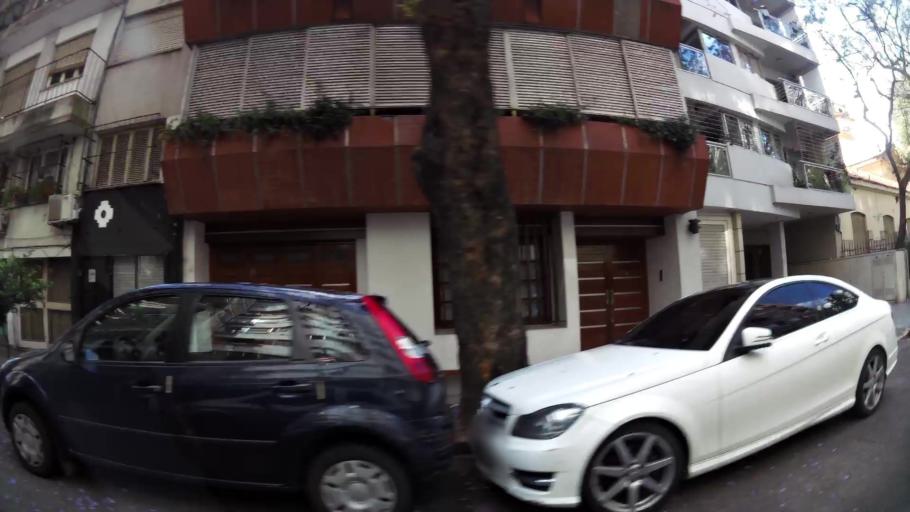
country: AR
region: Santa Fe
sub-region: Departamento de Rosario
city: Rosario
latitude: -32.9554
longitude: -60.6258
